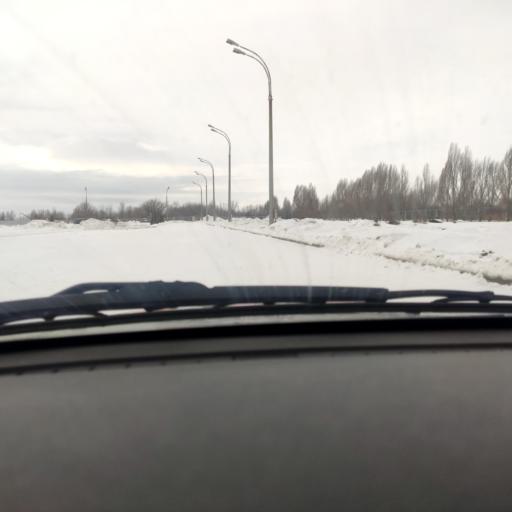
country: RU
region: Samara
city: Tol'yatti
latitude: 53.5534
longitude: 49.2499
